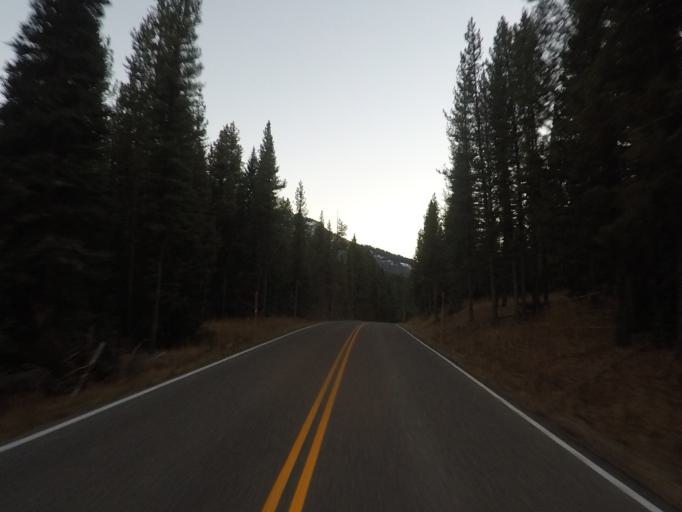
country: US
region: Montana
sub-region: Stillwater County
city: Absarokee
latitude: 44.9326
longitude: -110.0847
